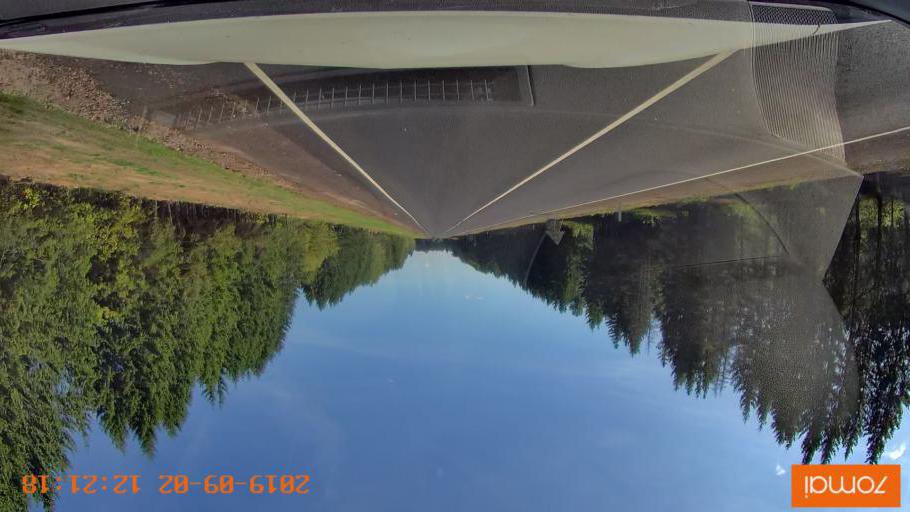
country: RU
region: Smolensk
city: Oster
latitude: 53.8885
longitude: 32.6585
